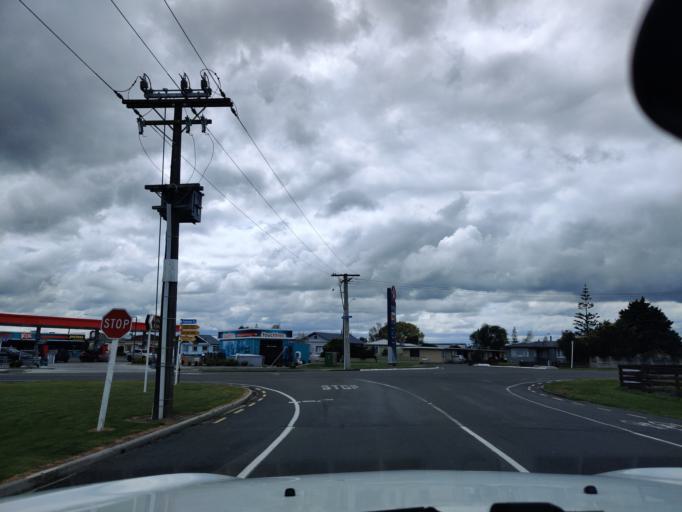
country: NZ
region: Manawatu-Wanganui
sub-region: Palmerston North City
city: Palmerston North
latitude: -40.2311
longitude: 175.5674
